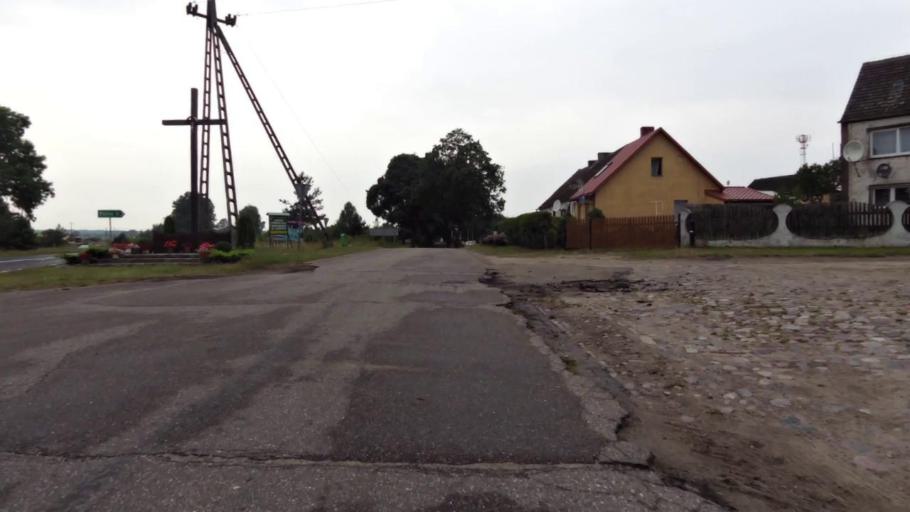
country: PL
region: West Pomeranian Voivodeship
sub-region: Powiat szczecinecki
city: Lubowo
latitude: 53.5869
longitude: 16.3821
